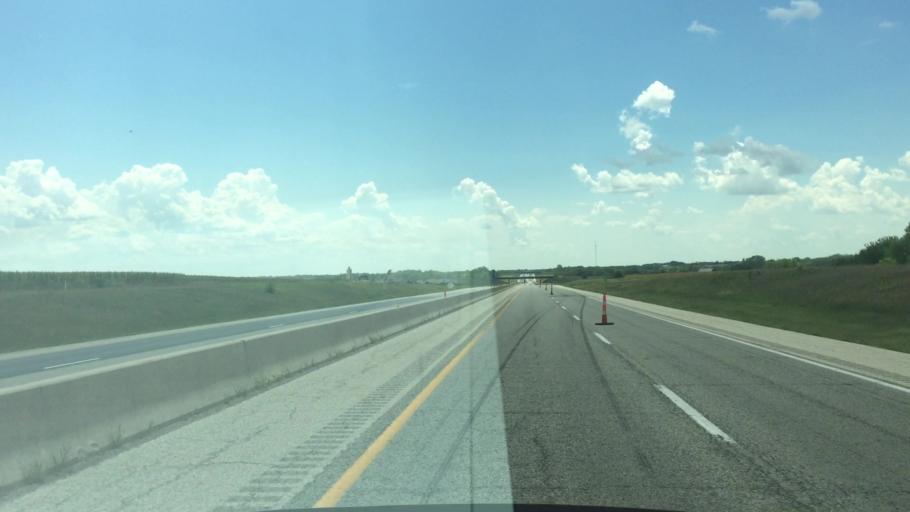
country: US
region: Kansas
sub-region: Osage County
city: Osage City
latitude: 38.7600
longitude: -95.9333
